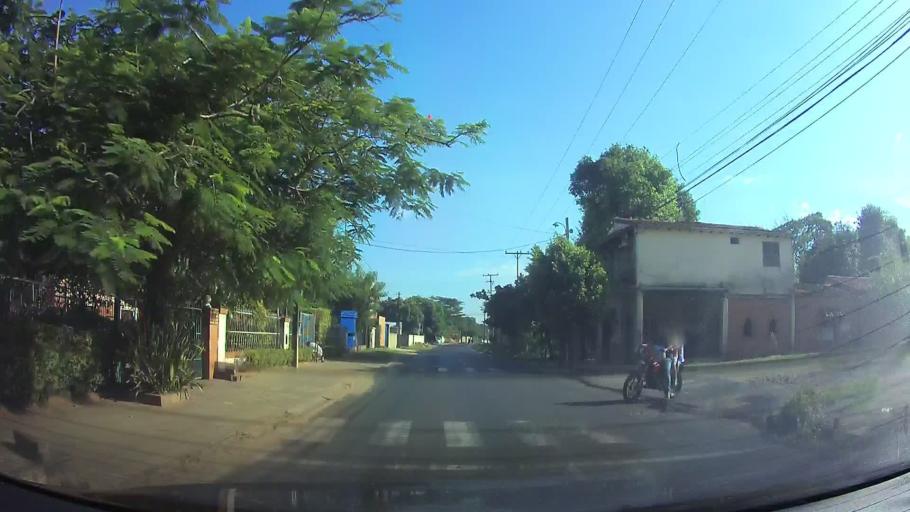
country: PY
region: Central
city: Fernando de la Mora
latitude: -25.2683
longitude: -57.5169
